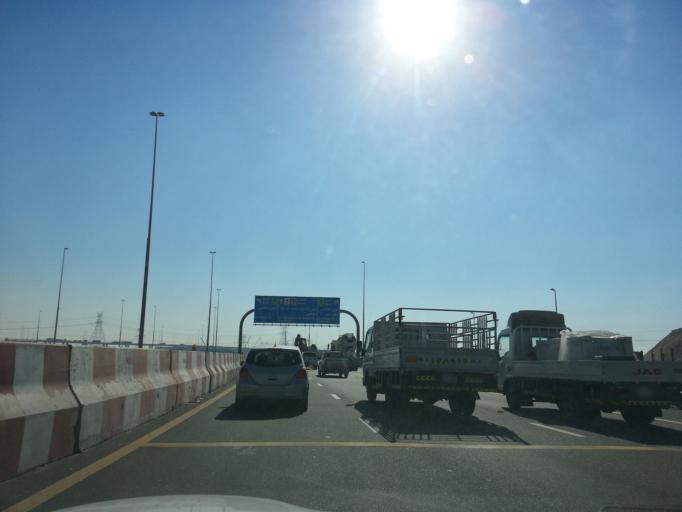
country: AE
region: Dubai
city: Dubai
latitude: 25.0244
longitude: 55.1637
